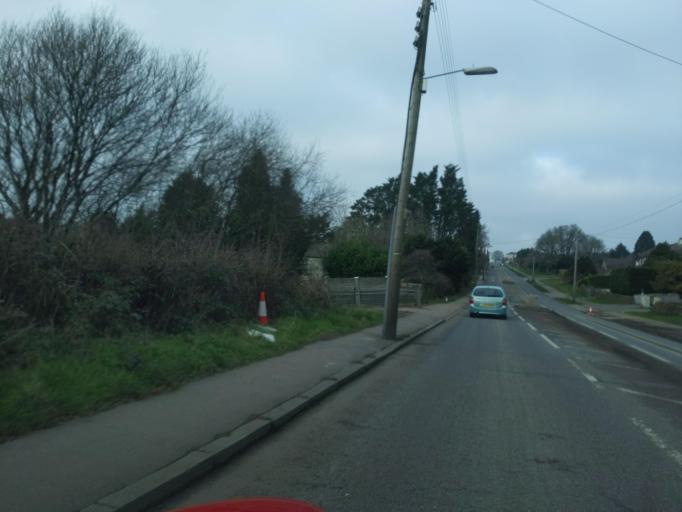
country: GB
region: England
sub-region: Cornwall
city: Callington
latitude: 50.5152
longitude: -4.3149
